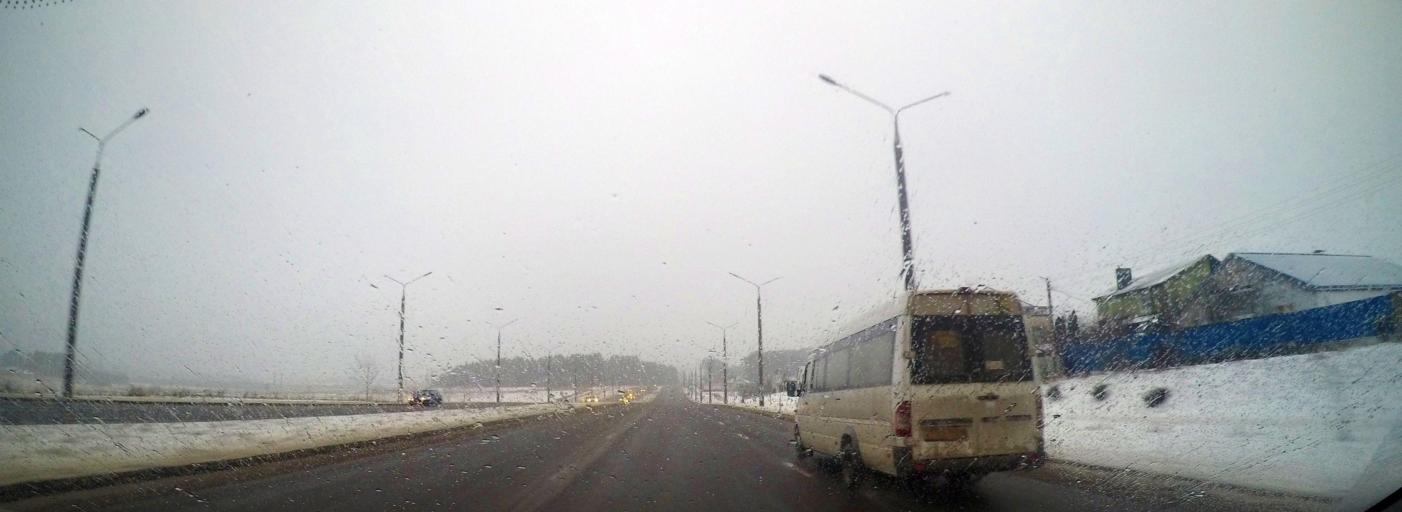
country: BY
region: Grodnenskaya
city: Hrodna
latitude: 53.6283
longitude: 23.8044
